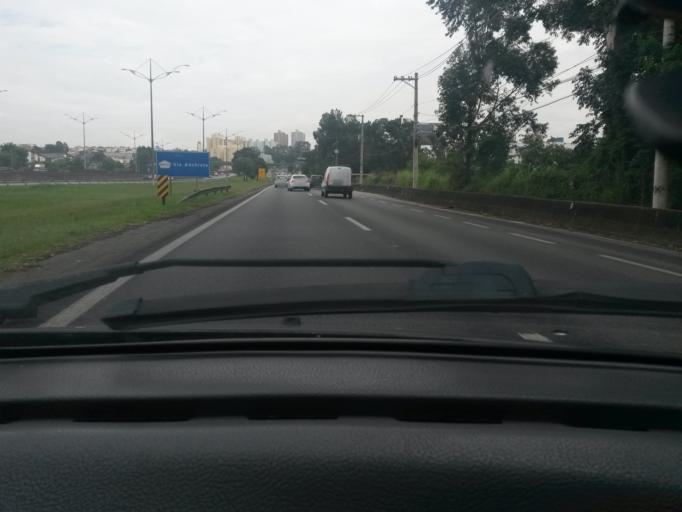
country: BR
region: Sao Paulo
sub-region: Sao Caetano Do Sul
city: Sao Caetano do Sul
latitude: -23.6398
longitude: -46.5902
